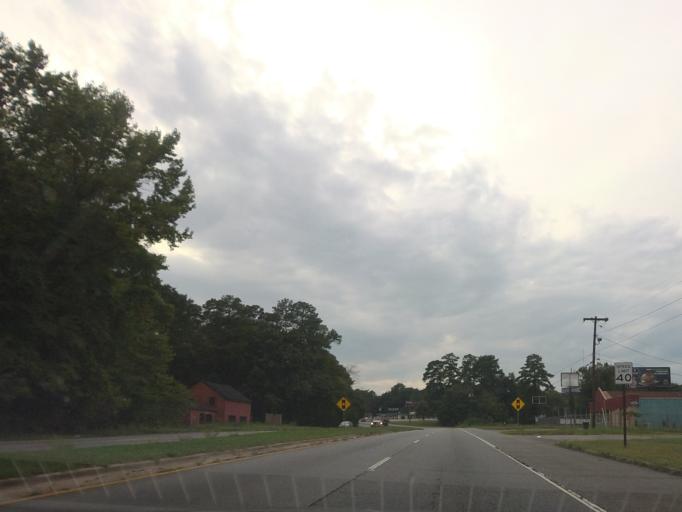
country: US
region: Georgia
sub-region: Bibb County
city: Macon
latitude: 32.8481
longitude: -83.5996
